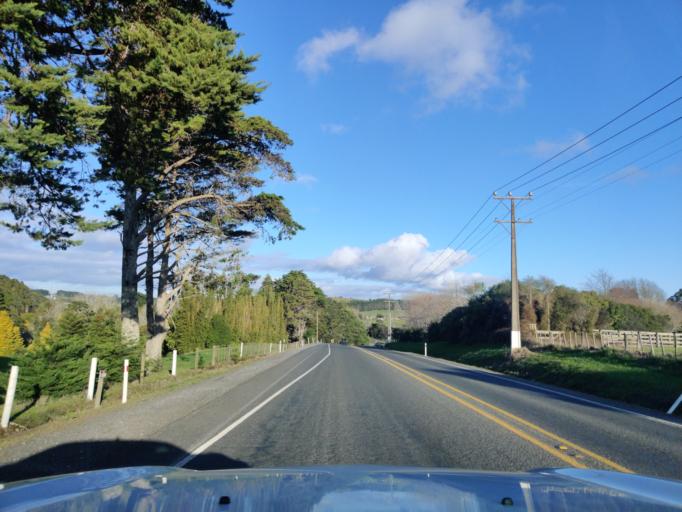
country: NZ
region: Auckland
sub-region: Auckland
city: Pakuranga
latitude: -36.9528
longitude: 174.9678
